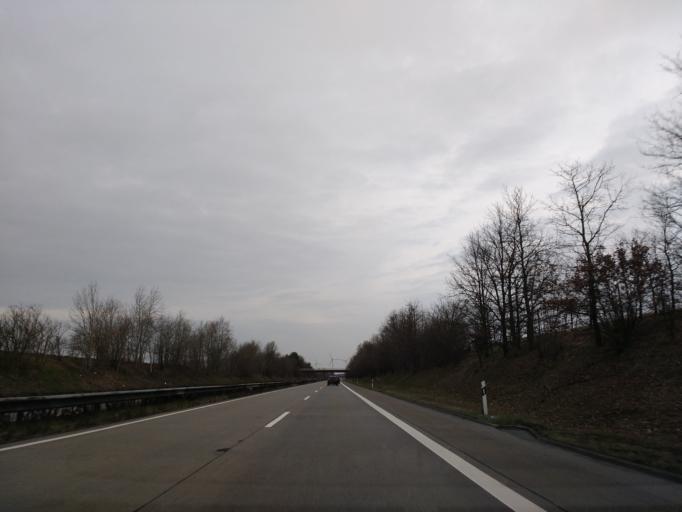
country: DE
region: Lower Saxony
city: Midlum
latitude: 53.6557
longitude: 8.6604
